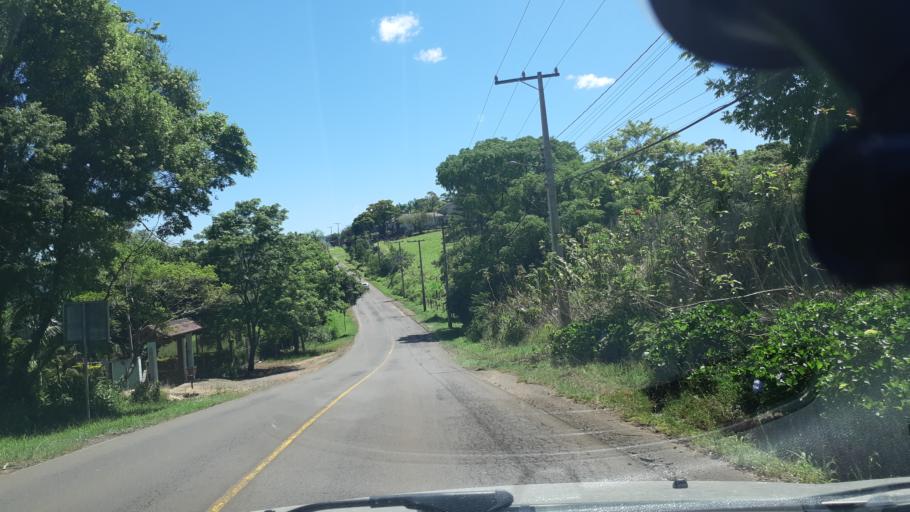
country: BR
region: Rio Grande do Sul
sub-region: Novo Hamburgo
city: Novo Hamburgo
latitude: -29.6232
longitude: -51.0936
